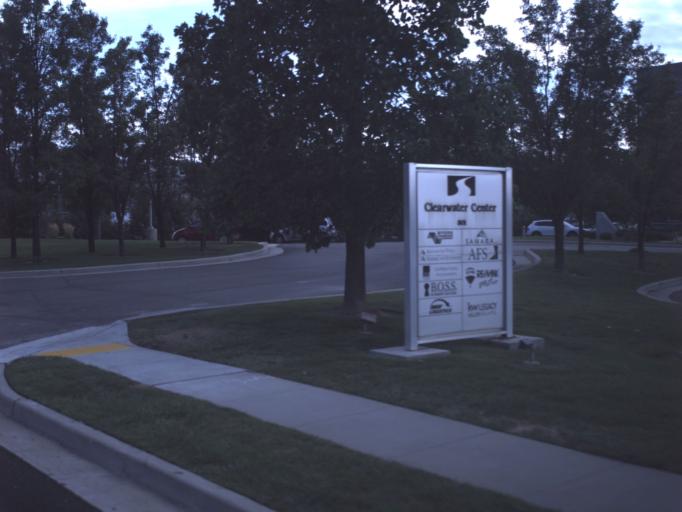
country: US
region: Utah
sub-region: Davis County
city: West Bountiful
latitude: 40.8981
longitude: -111.8923
